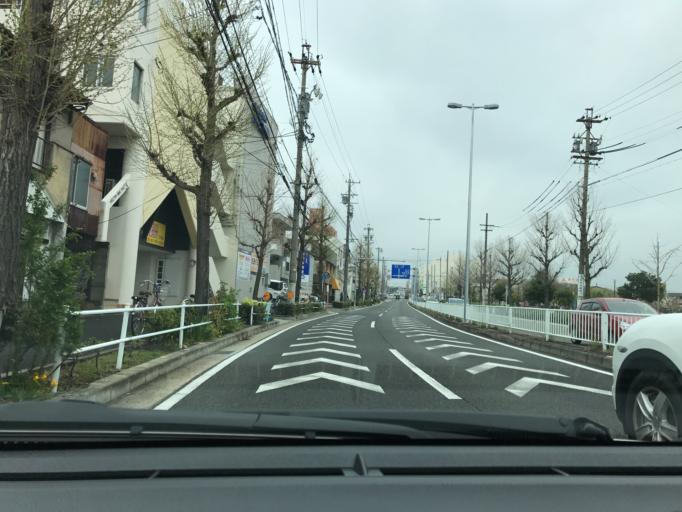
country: JP
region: Aichi
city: Nagoya-shi
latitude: 35.1508
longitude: 136.9506
